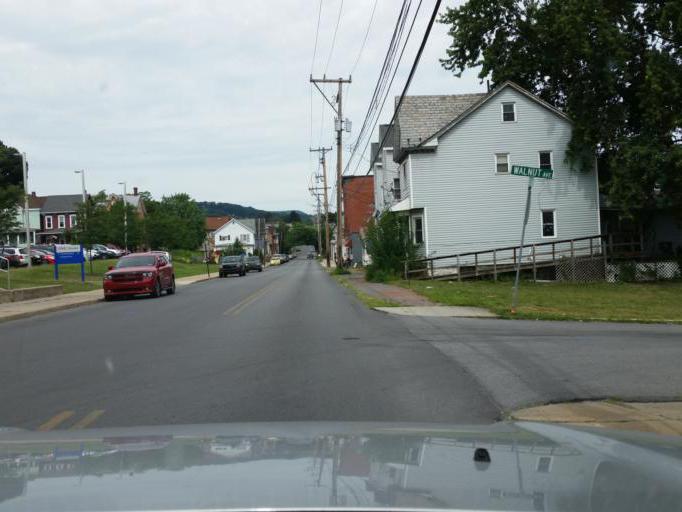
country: US
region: Pennsylvania
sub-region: Blair County
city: Altoona
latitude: 40.5236
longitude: -78.3971
